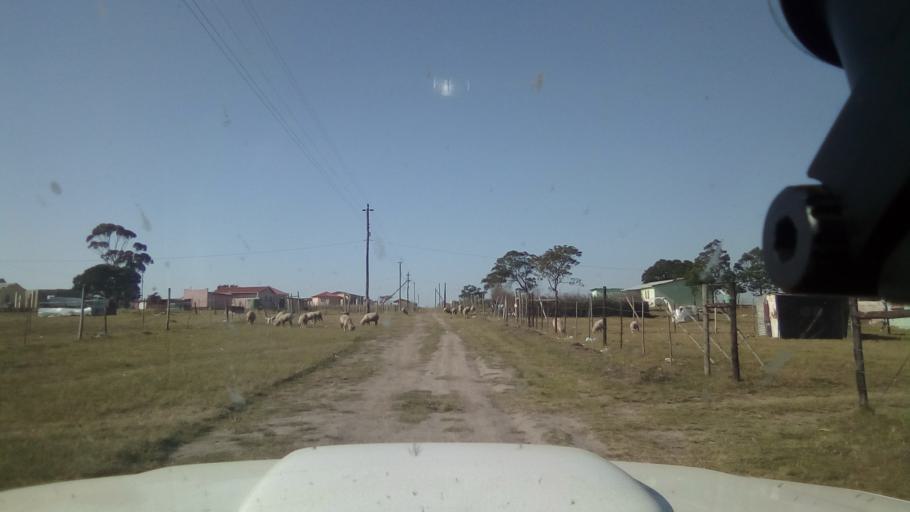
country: ZA
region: Eastern Cape
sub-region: Buffalo City Metropolitan Municipality
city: Bhisho
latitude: -32.9419
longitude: 27.3297
